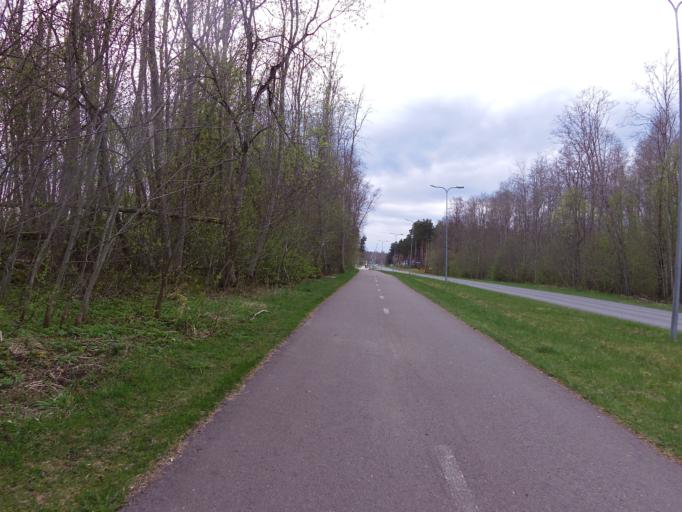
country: EE
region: Harju
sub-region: Kiili vald
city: Kiili
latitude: 59.3631
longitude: 24.8162
